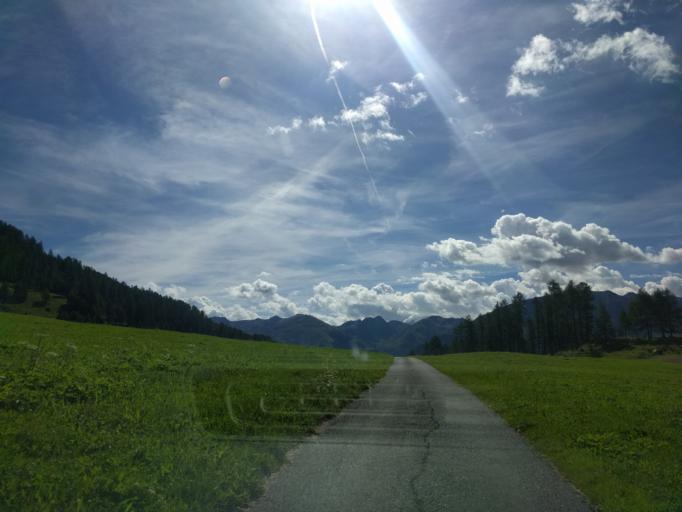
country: IT
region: Trentino-Alto Adige
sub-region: Bolzano
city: Tubre
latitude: 46.6237
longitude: 10.3638
